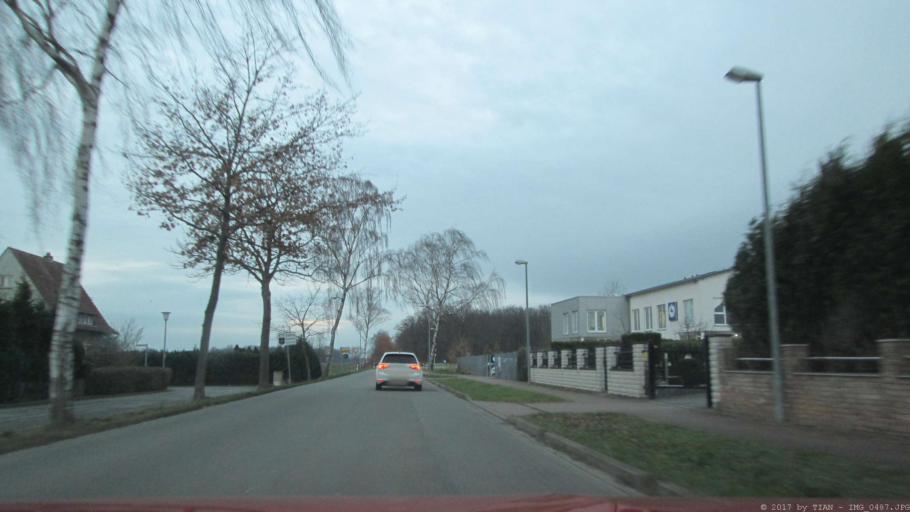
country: DE
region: Lower Saxony
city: Wolfsburg
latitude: 52.4477
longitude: 10.7741
